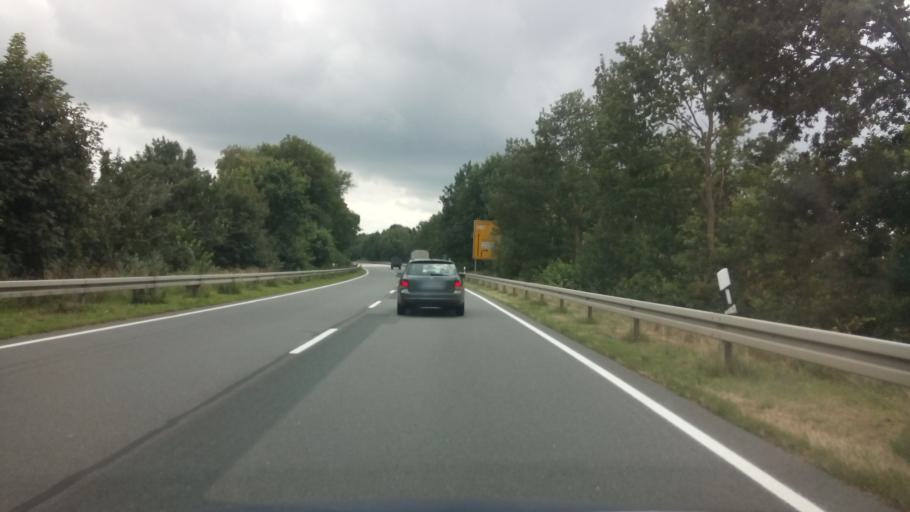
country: DE
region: Lower Saxony
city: Diepholz
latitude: 52.5982
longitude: 8.3536
